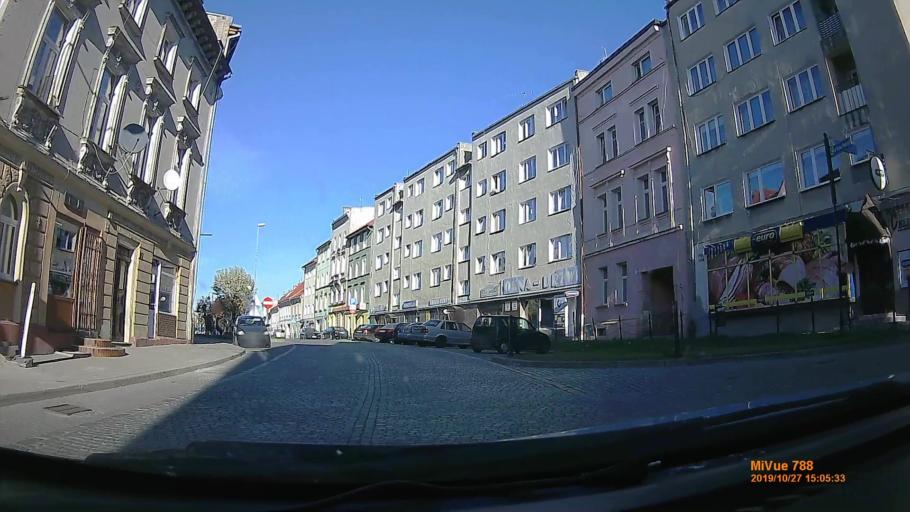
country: PL
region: Lower Silesian Voivodeship
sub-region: Powiat klodzki
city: Miedzylesie
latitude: 50.1462
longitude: 16.6658
